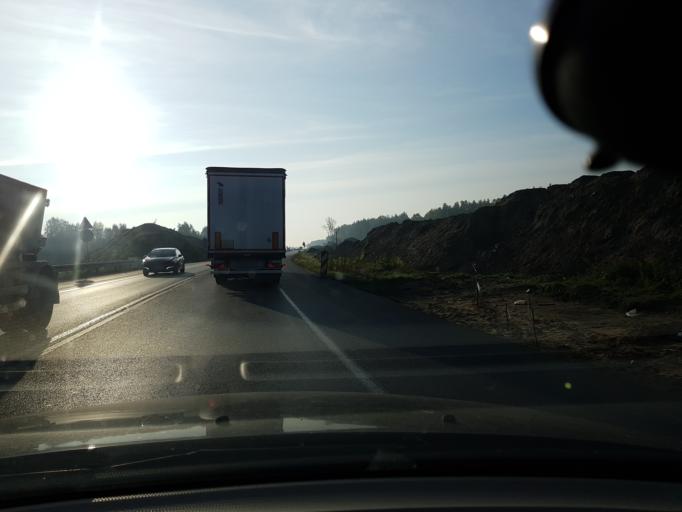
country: PL
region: Masovian Voivodeship
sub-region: Powiat otwocki
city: Jozefow
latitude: 52.1645
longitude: 21.2987
